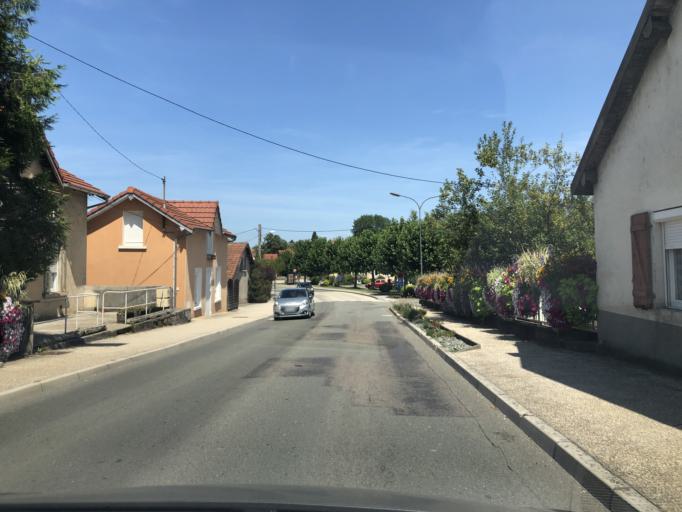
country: FR
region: Franche-Comte
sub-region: Departement du Doubs
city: Voujeaucourt
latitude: 47.4751
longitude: 6.7661
